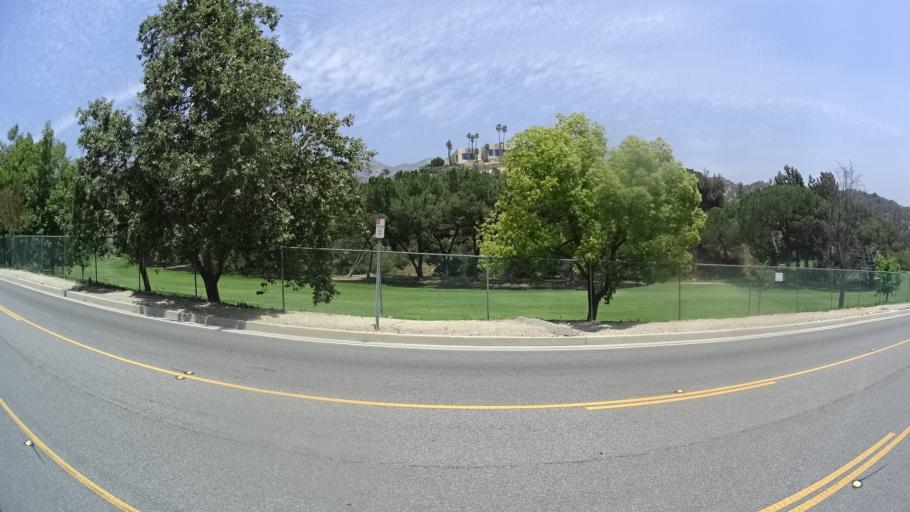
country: US
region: California
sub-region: Los Angeles County
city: Burbank
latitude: 34.2037
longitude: -118.3055
